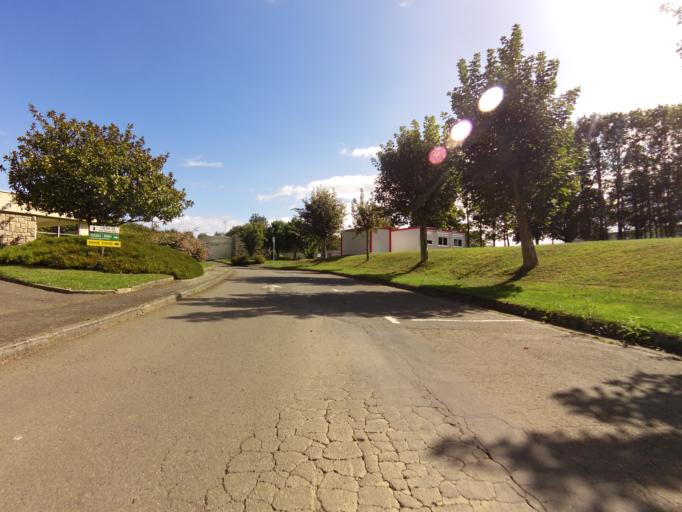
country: FR
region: Brittany
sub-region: Departement des Cotes-d'Armor
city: Langueux
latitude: 48.4905
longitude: -2.7486
